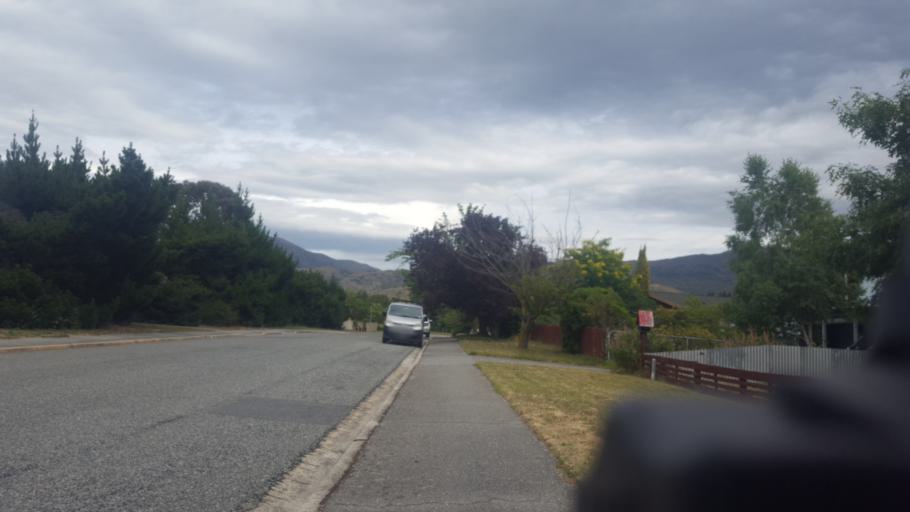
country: NZ
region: Otago
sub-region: Queenstown-Lakes District
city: Wanaka
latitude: -45.0414
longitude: 169.1995
